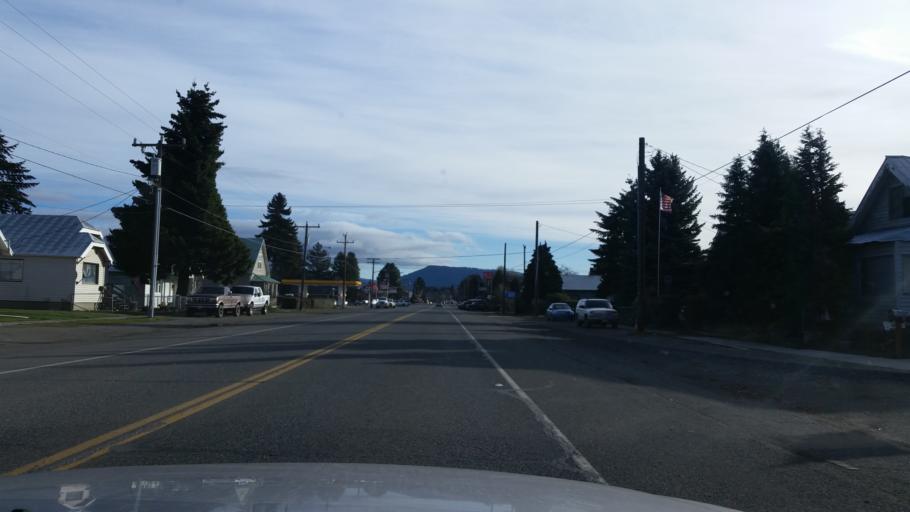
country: US
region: Washington
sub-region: Kittitas County
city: Cle Elum
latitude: 47.1930
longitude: -120.9231
